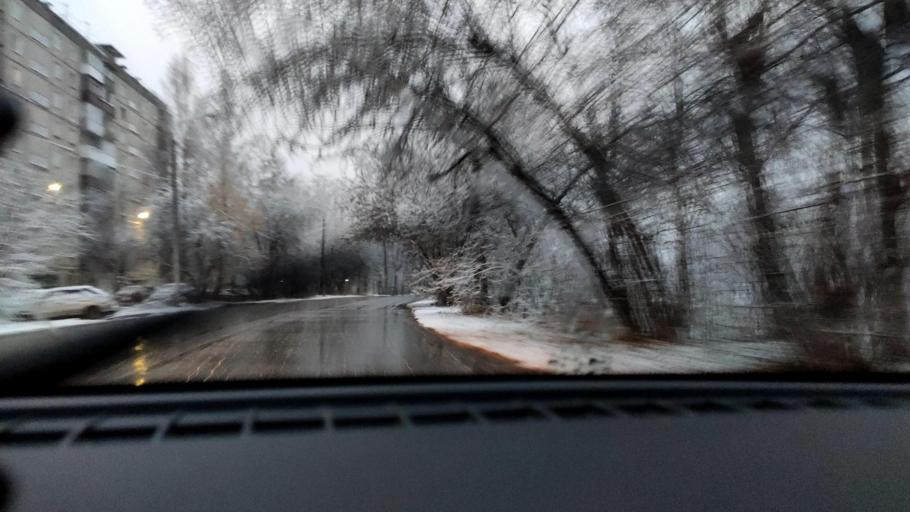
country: RU
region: Perm
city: Overyata
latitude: 58.0184
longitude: 55.9717
